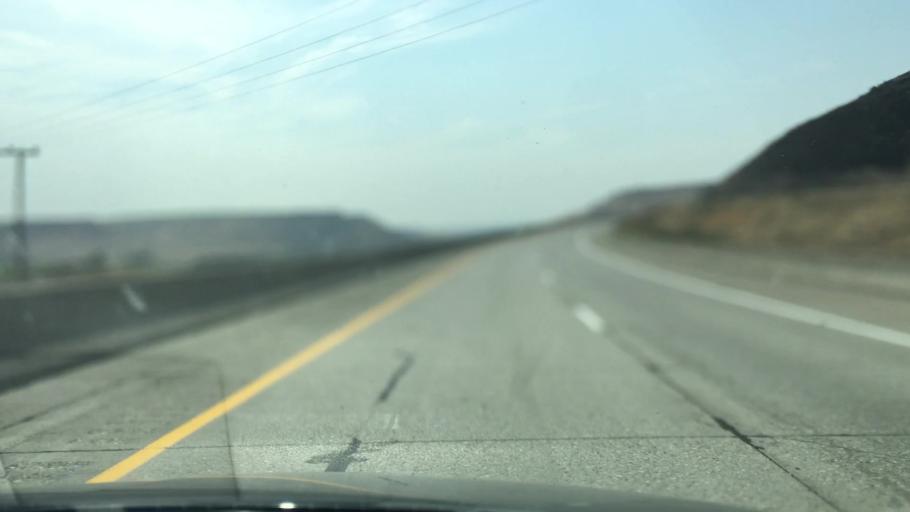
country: US
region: Idaho
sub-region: Elmore County
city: Glenns Ferry
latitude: 42.9577
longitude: -115.3492
